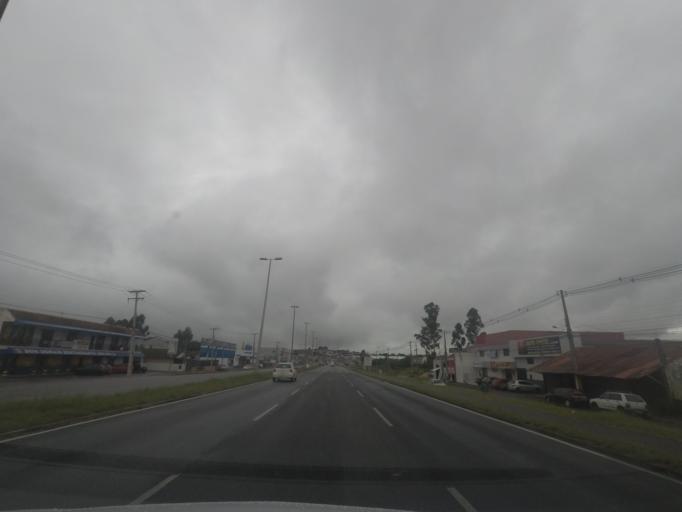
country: BR
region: Parana
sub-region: Colombo
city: Colombo
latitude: -25.3483
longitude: -49.1722
